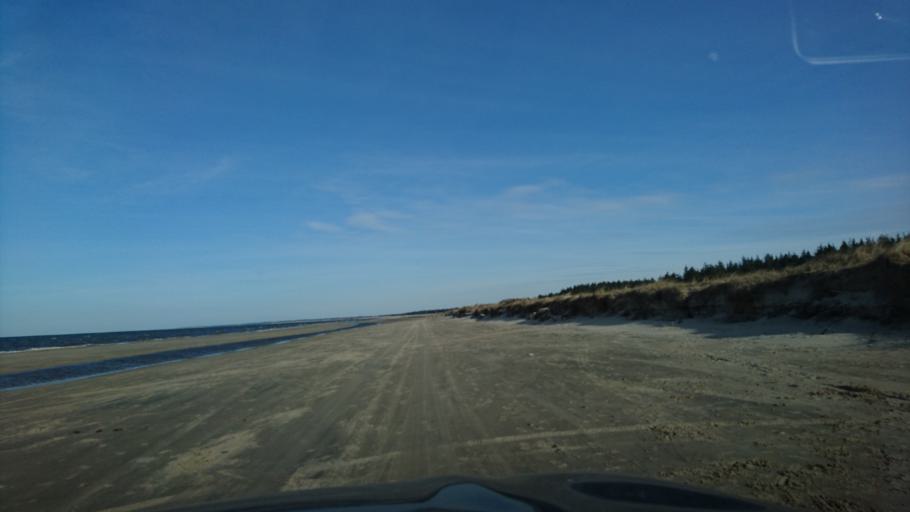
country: DK
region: North Denmark
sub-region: Hjorring Kommune
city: Hirtshals
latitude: 57.5910
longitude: 10.0527
